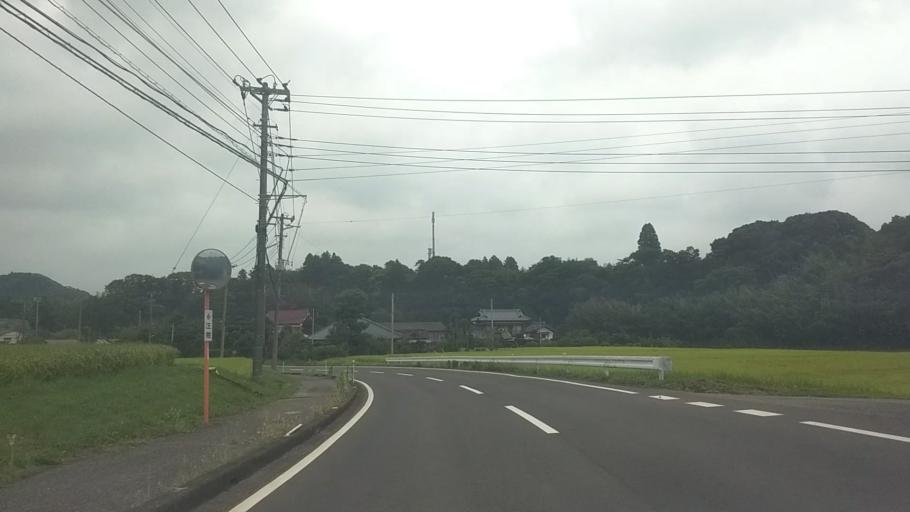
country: JP
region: Chiba
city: Kawaguchi
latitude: 35.2537
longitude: 140.0424
